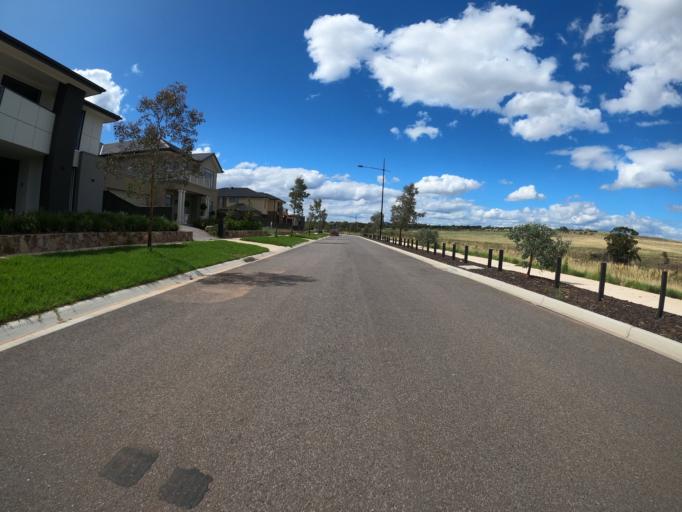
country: AU
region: Victoria
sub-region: Hume
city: Greenvale
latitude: -37.6131
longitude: 144.8912
